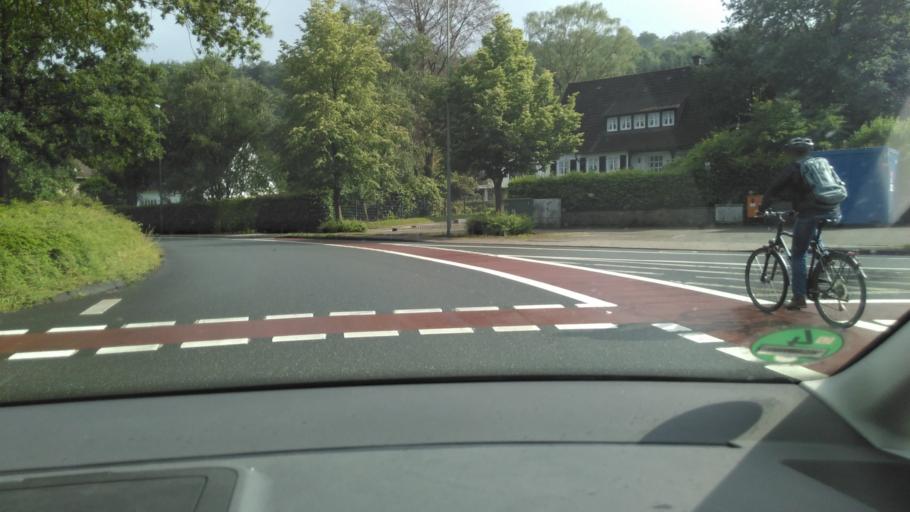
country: DE
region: North Rhine-Westphalia
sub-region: Regierungsbezirk Detmold
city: Bielefeld
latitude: 52.0327
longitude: 8.4997
